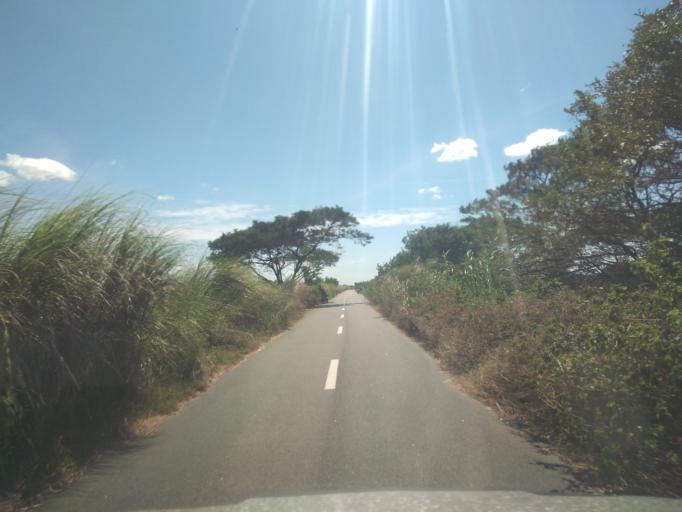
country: PH
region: Central Luzon
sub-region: Province of Pampanga
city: San Basilio
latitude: 15.0336
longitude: 120.5971
